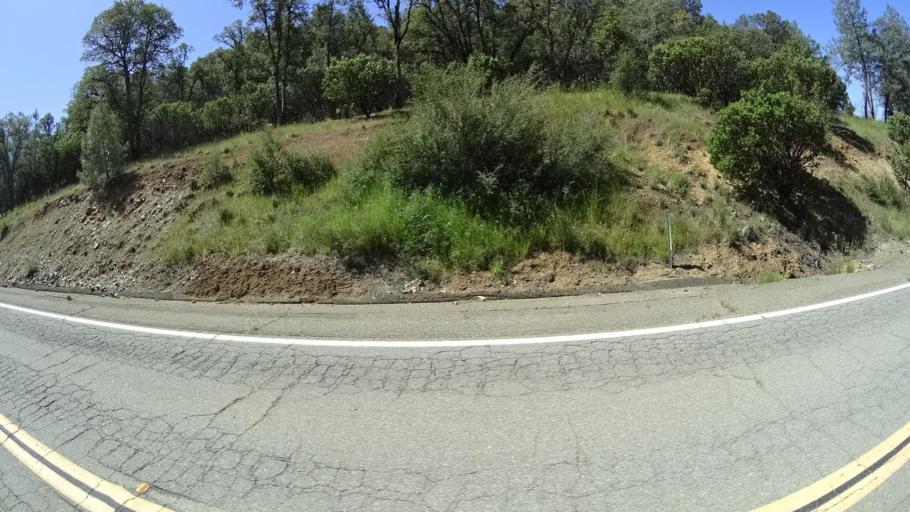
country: US
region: California
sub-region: Lake County
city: Hidden Valley Lake
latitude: 38.8926
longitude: -122.4833
